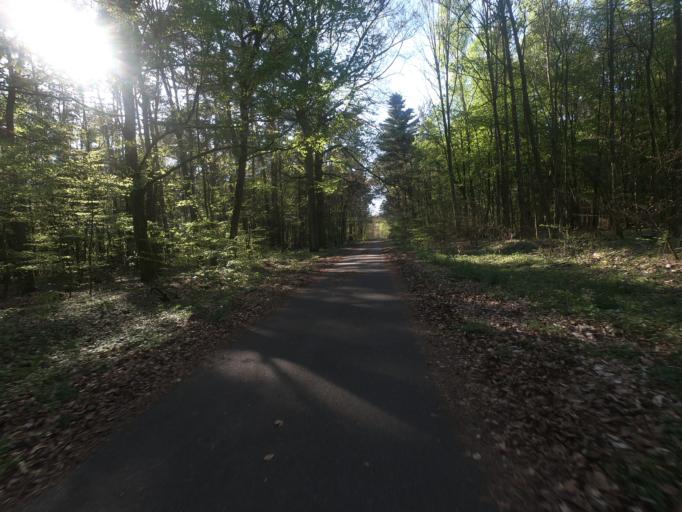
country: DE
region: Hesse
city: Langen
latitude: 49.9982
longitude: 8.6321
